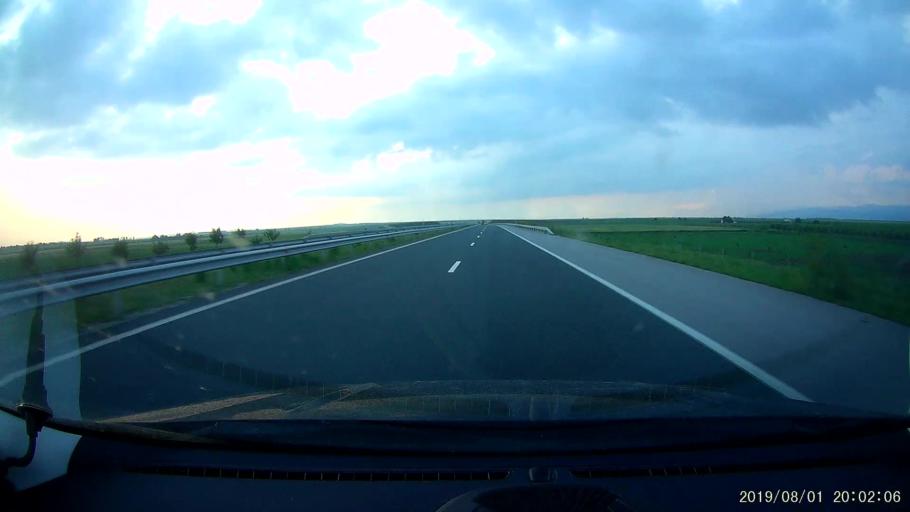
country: BG
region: Yambol
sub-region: Obshtina Straldzha
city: Straldzha
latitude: 42.5584
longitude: 26.6413
